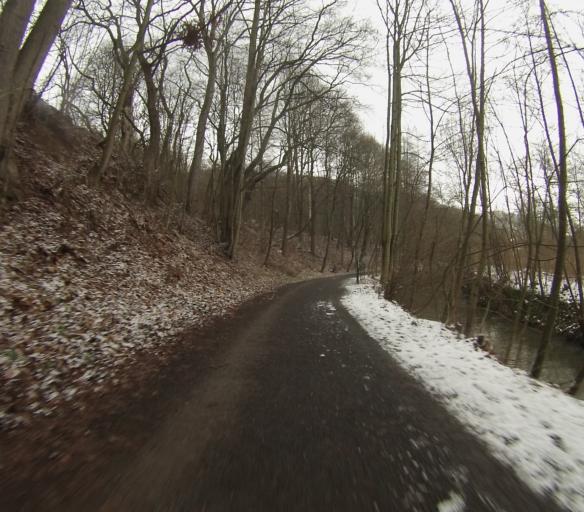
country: CZ
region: Ustecky
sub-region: Okres Decin
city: Decin
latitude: 50.7600
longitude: 14.2550
